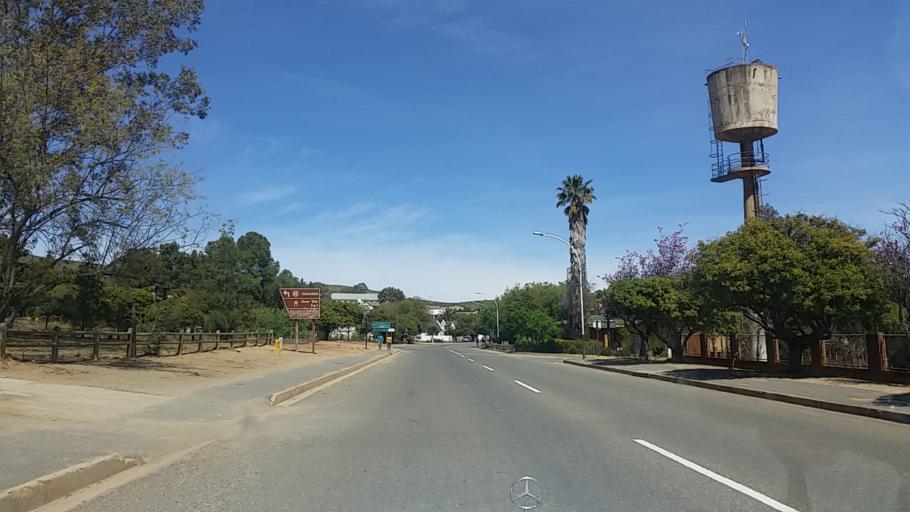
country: ZA
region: Western Cape
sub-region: Eden District Municipality
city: Knysna
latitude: -33.6580
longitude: 23.1243
